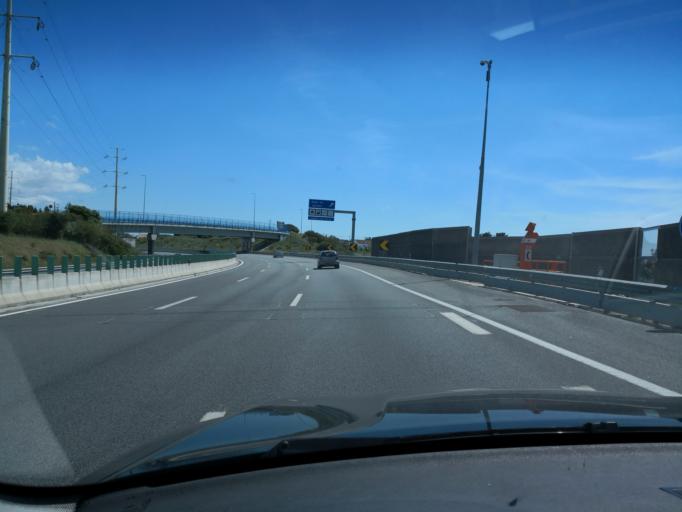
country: PT
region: Setubal
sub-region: Almada
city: Sobreda
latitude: 38.6421
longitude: -9.2019
